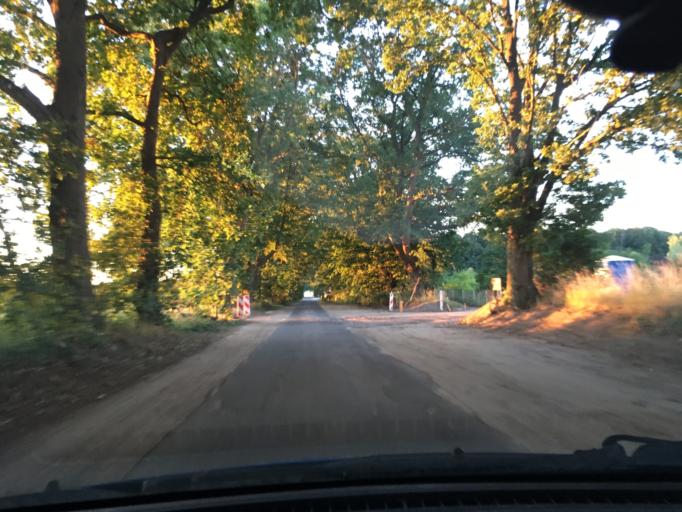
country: DE
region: Lower Saxony
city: Adendorf
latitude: 53.2927
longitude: 10.4488
